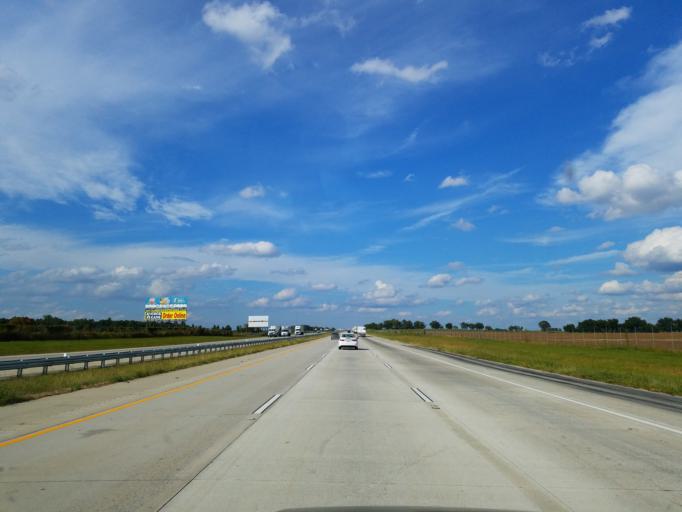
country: US
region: Georgia
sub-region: Dooly County
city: Vienna
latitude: 32.1482
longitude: -83.7565
